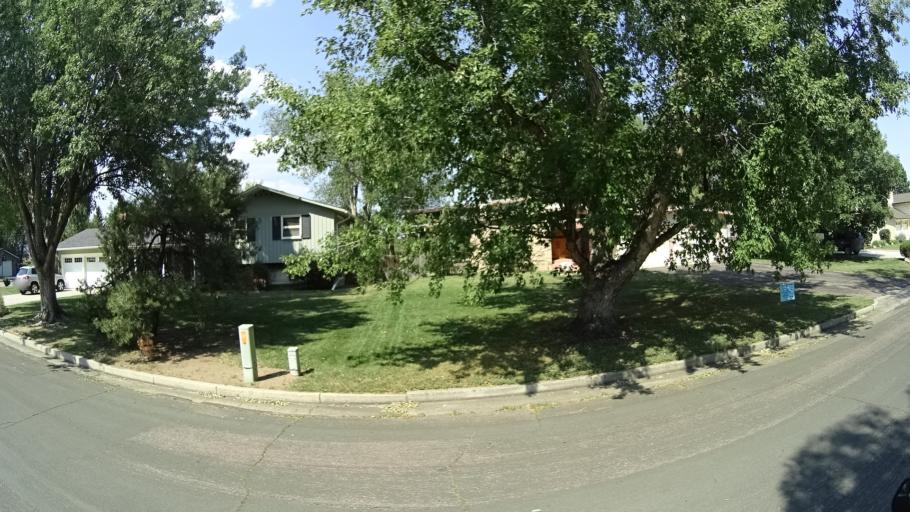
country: US
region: Colorado
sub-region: El Paso County
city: Colorado Springs
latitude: 38.8010
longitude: -104.8295
